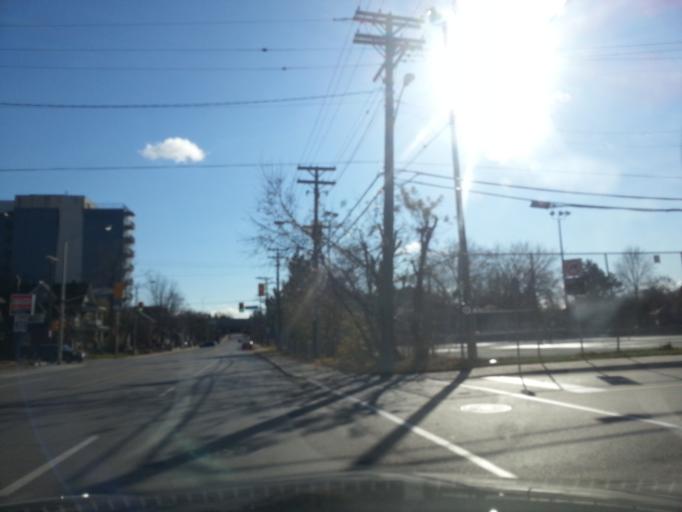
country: CA
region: Ontario
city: Ottawa
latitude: 45.3981
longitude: -75.7310
